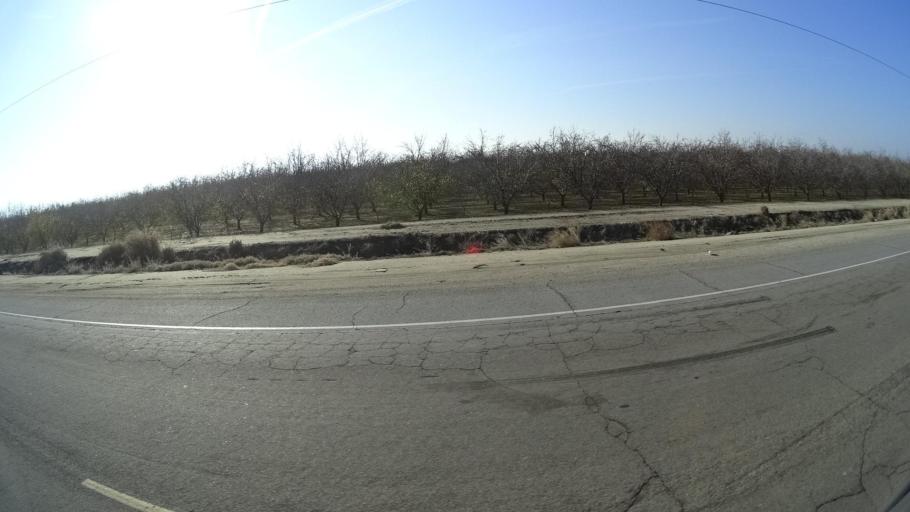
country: US
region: California
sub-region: Kern County
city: Greenfield
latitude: 35.2523
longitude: -118.9960
